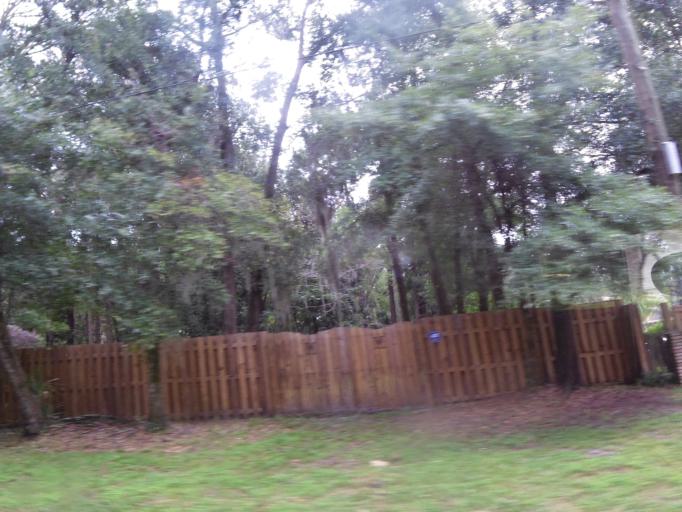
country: US
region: Florida
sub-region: Clay County
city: Bellair-Meadowbrook Terrace
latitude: 30.2560
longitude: -81.7206
